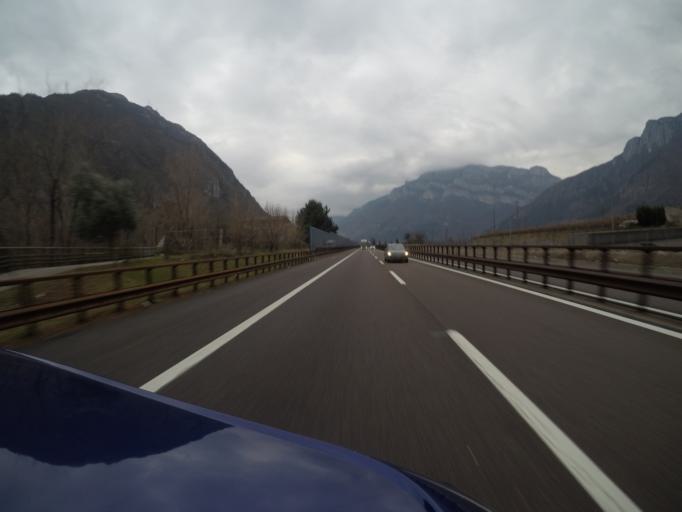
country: IT
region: Trentino-Alto Adige
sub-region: Provincia di Trento
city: Sabbionara
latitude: 45.7418
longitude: 10.9719
